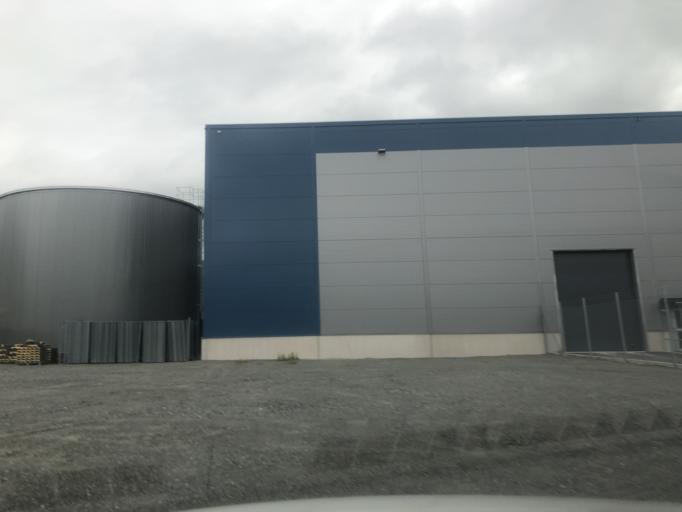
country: SE
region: Vaestra Goetaland
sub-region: Goteborg
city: Majorna
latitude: 57.7340
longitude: 11.8673
